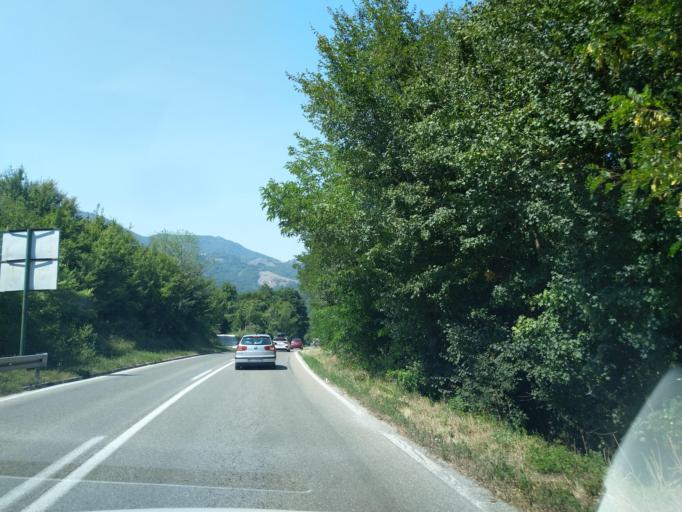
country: RS
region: Central Serbia
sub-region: Zlatiborski Okrug
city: Prijepolje
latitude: 43.4680
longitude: 19.6669
